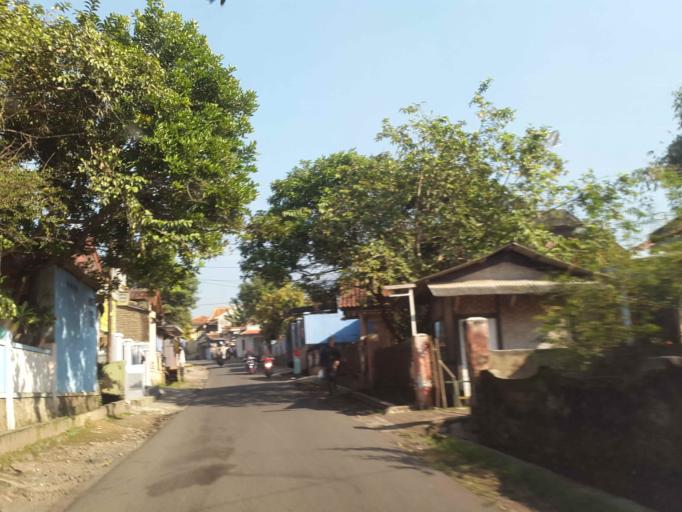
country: ID
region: West Java
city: Cibeber
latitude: -6.8665
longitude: 107.0870
